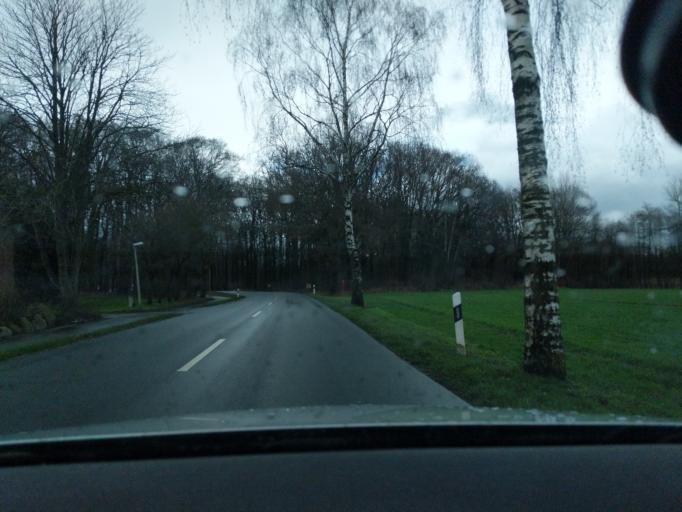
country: DE
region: Lower Saxony
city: Deinste
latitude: 53.5281
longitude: 9.4297
